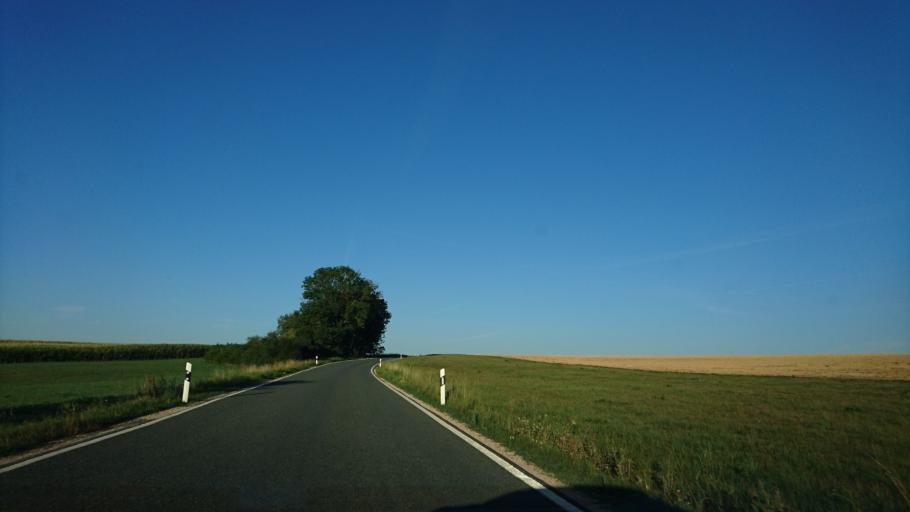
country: DE
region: Bavaria
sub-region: Regierungsbezirk Mittelfranken
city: Nennslingen
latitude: 49.0515
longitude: 11.1589
